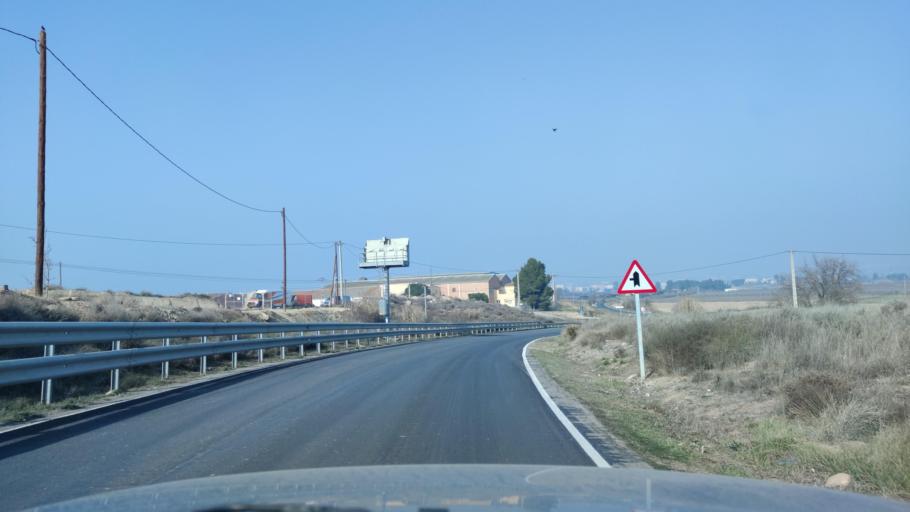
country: ES
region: Catalonia
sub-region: Provincia de Lleida
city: Alfes
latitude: 41.5595
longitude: 0.6156
